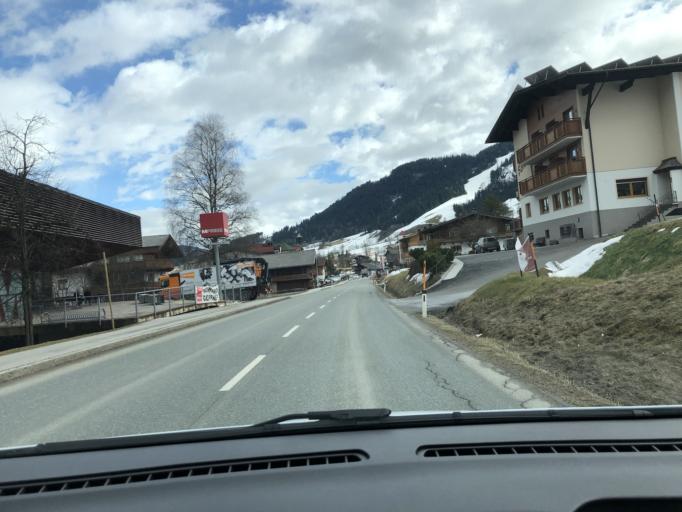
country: AT
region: Tyrol
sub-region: Politischer Bezirk Kufstein
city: Worgl
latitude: 47.4492
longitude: 12.0825
